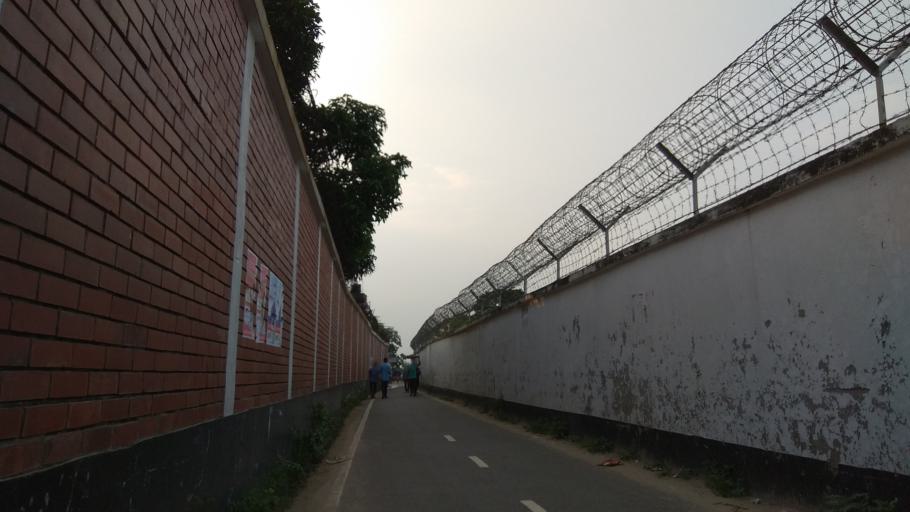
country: BD
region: Dhaka
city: Tungi
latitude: 23.8537
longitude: 90.3874
